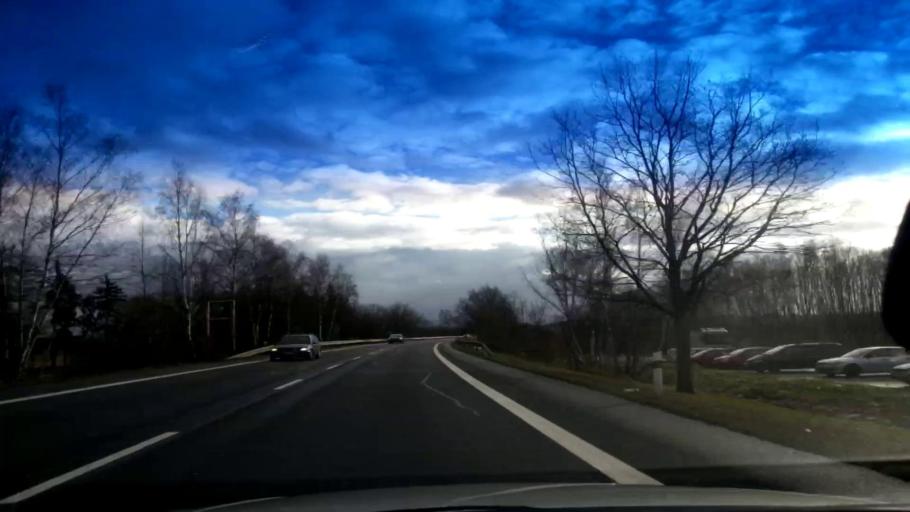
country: CZ
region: Karlovarsky
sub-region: Okres Cheb
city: Frantiskovy Lazne
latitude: 50.1197
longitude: 12.3713
